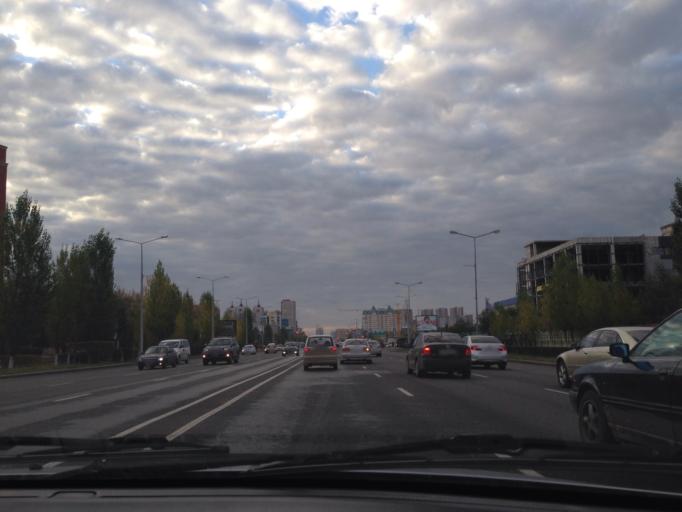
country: KZ
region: Astana Qalasy
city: Astana
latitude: 51.1482
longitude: 71.4584
